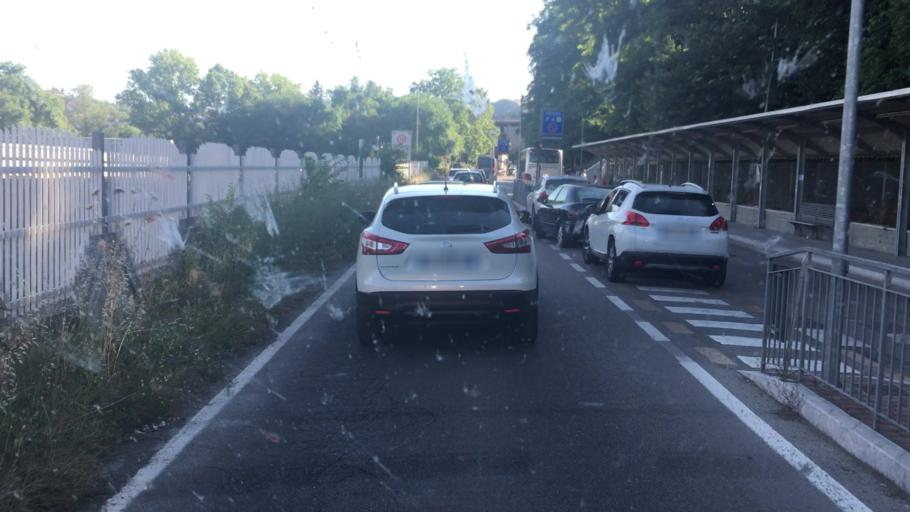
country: IT
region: Basilicate
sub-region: Provincia di Potenza
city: Potenza
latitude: 40.6295
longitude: 15.8078
